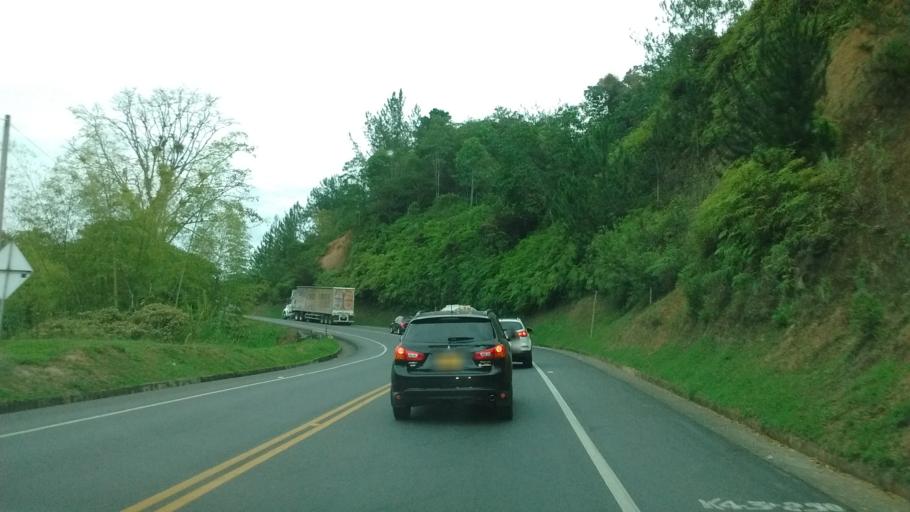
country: CO
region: Cauca
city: Caldono
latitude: 2.7953
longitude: -76.5528
